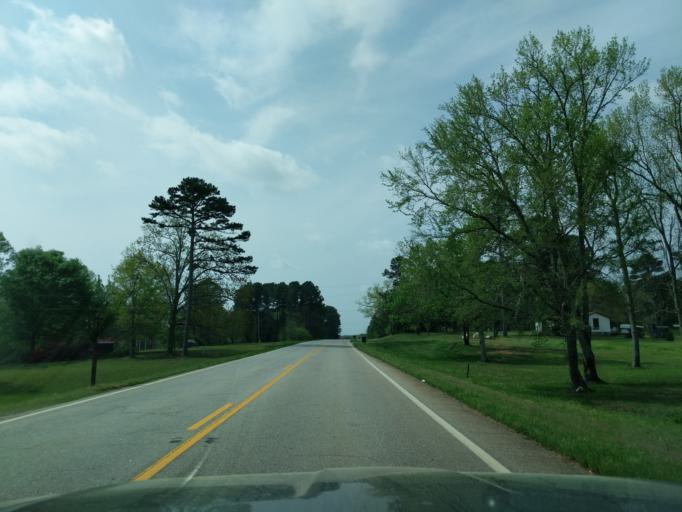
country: US
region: Georgia
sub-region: Lincoln County
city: Lincolnton
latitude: 33.7671
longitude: -82.3756
